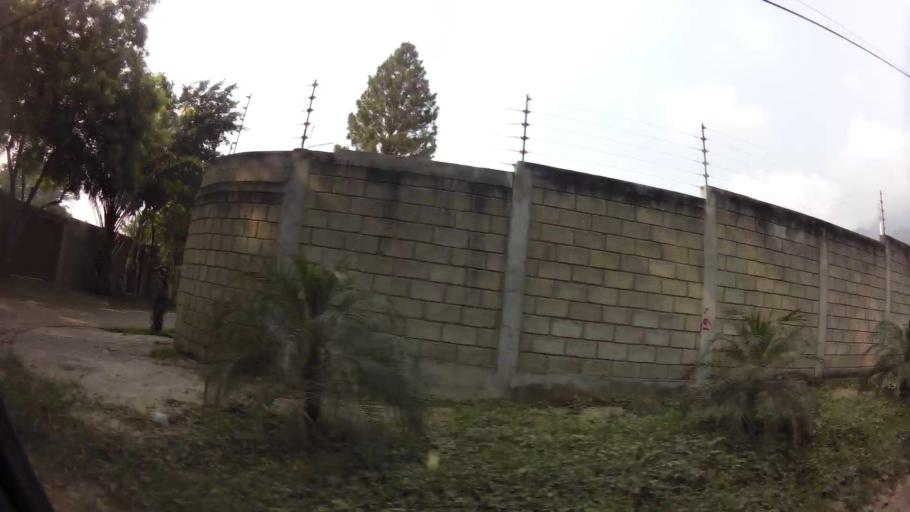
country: HN
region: Cortes
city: El Zapotal del Norte
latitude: 15.5195
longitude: -88.0445
